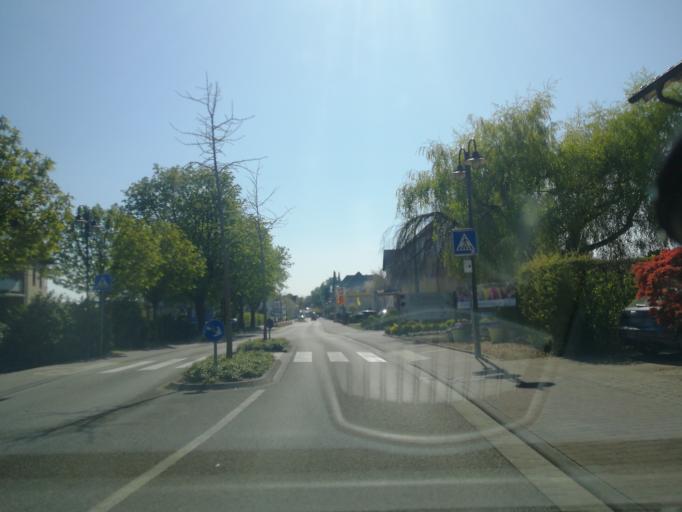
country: DE
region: Lower Saxony
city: Bad Rothenfelde
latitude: 52.1142
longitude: 8.1627
